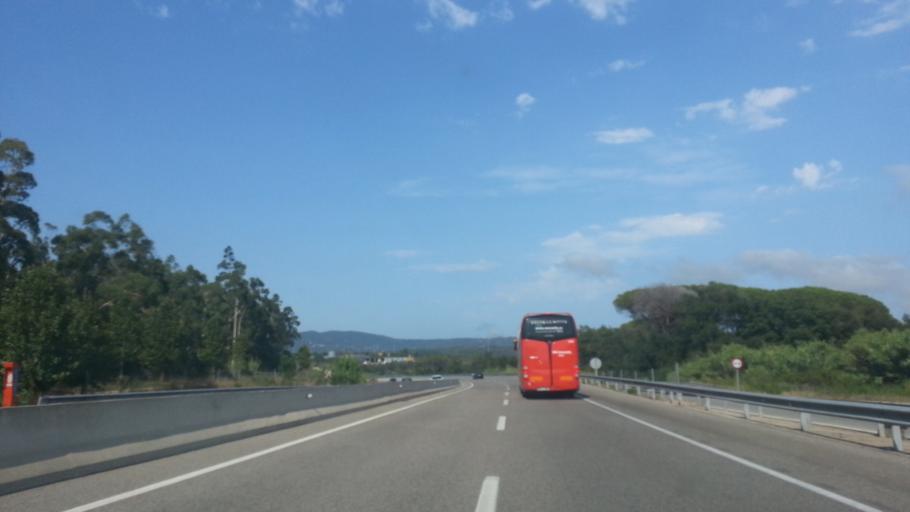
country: ES
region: Catalonia
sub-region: Provincia de Girona
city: Llagostera
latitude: 41.8248
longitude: 2.9161
